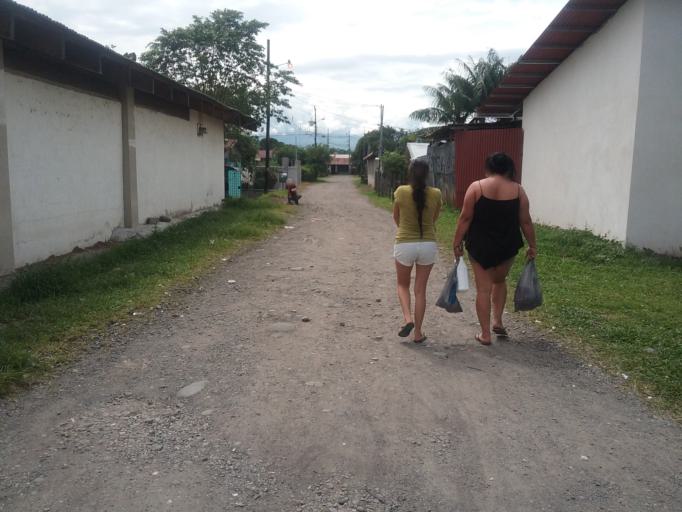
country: CR
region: Limon
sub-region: Canton de Pococi
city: Guapiles
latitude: 10.3201
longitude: -83.8864
